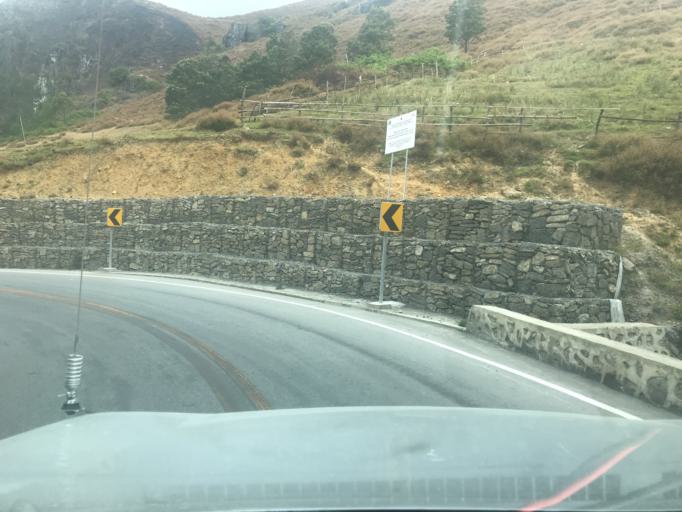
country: TL
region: Manufahi
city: Same
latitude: -8.8830
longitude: 125.6022
